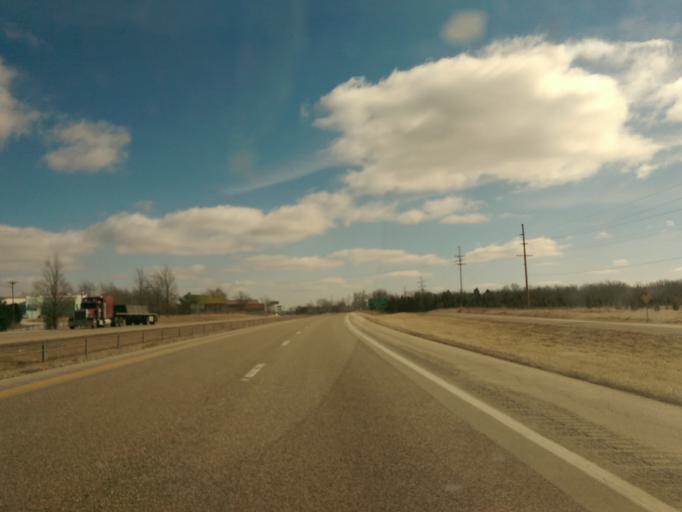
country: US
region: Missouri
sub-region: Montgomery County
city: Montgomery City
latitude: 38.8802
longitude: -91.3907
